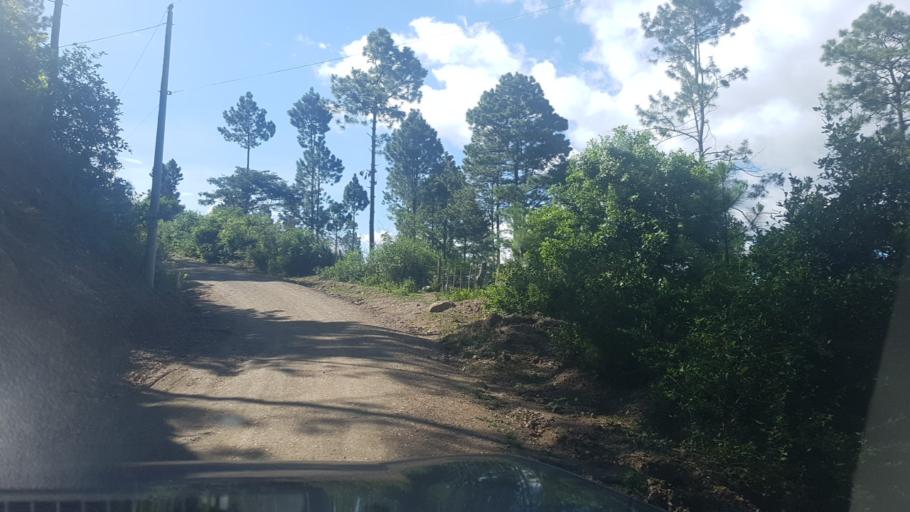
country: NI
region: Nueva Segovia
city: Ocotal
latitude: 13.6433
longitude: -86.6384
